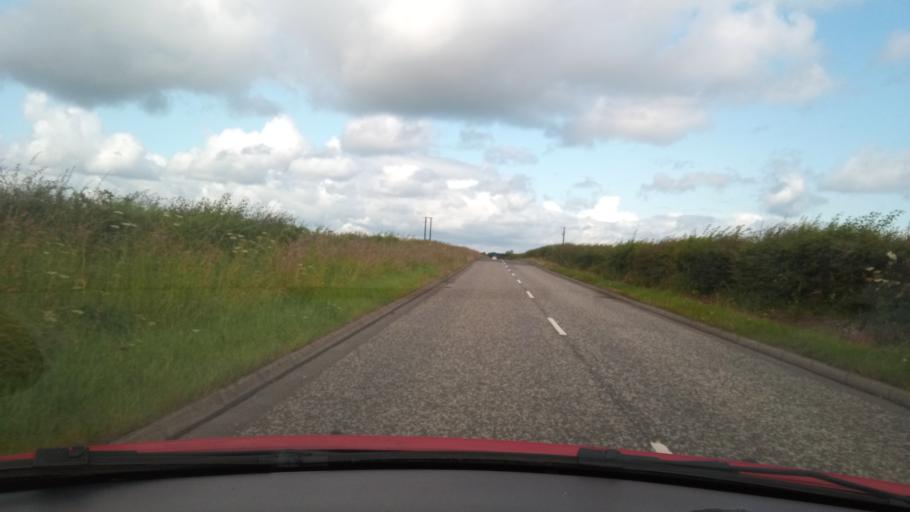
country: GB
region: Scotland
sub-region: East Lothian
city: Ormiston
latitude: 55.9324
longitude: -2.9279
